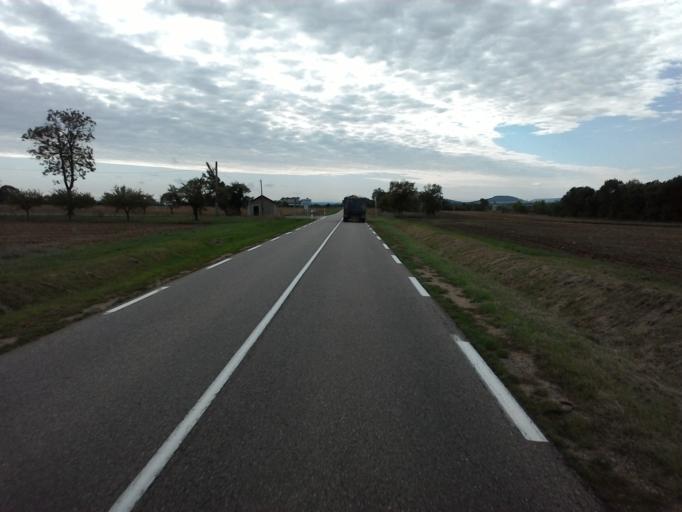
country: FR
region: Lorraine
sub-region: Departement de Meurthe-et-Moselle
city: Ecrouves
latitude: 48.7783
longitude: 5.8631
